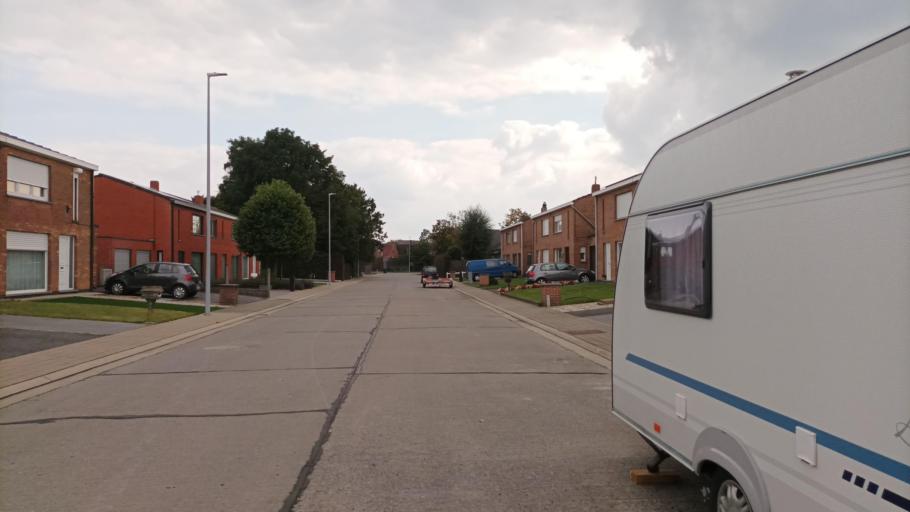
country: BE
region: Flanders
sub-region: Provincie West-Vlaanderen
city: Wevelgem
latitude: 50.8215
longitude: 3.1660
